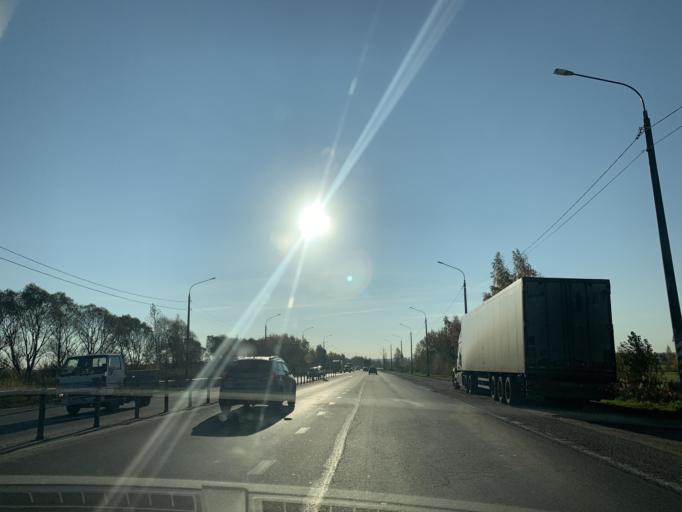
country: RU
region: Jaroslavl
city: Yaroslavl
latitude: 57.6204
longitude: 39.7735
